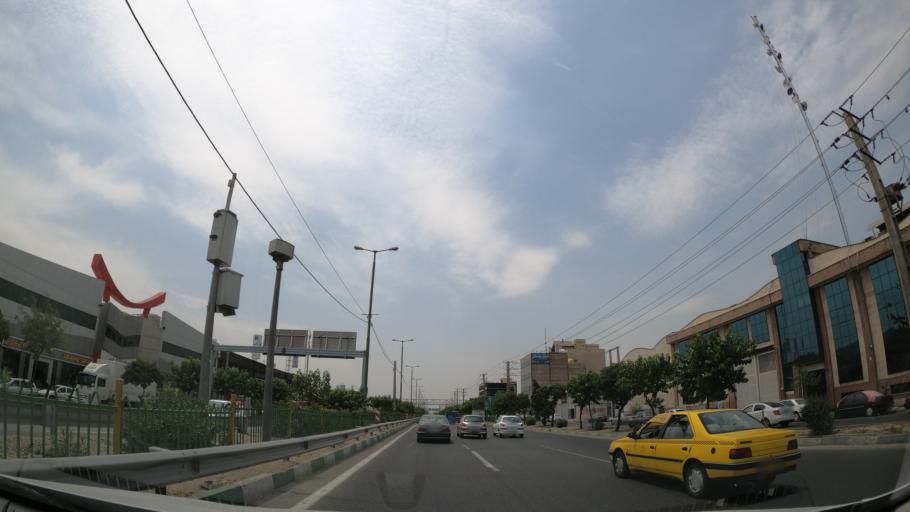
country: IR
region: Tehran
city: Tehran
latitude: 35.6760
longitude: 51.3010
